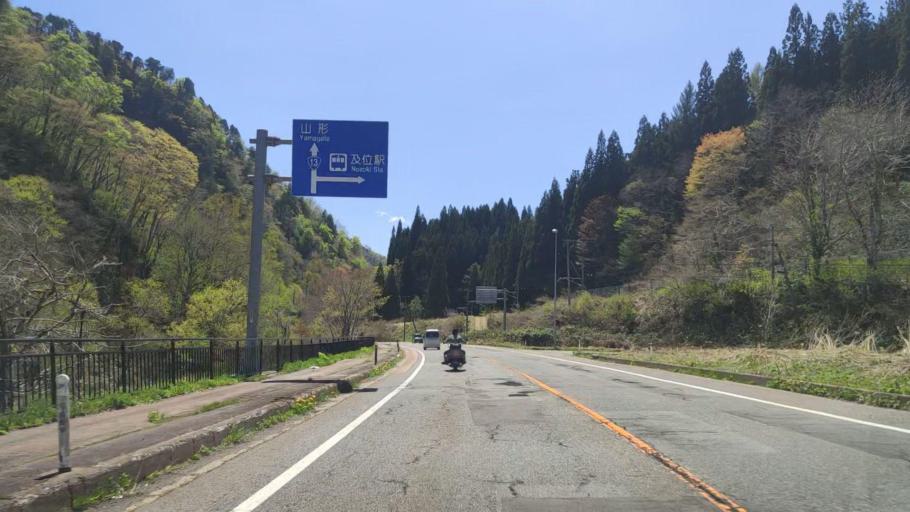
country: JP
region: Akita
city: Yuzawa
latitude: 38.9886
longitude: 140.3625
